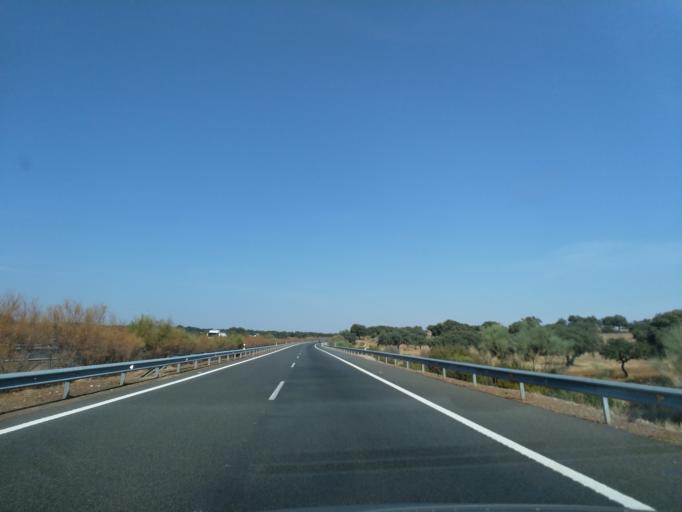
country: ES
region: Extremadura
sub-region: Provincia de Badajoz
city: Mirandilla
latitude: 38.9965
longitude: -6.3301
